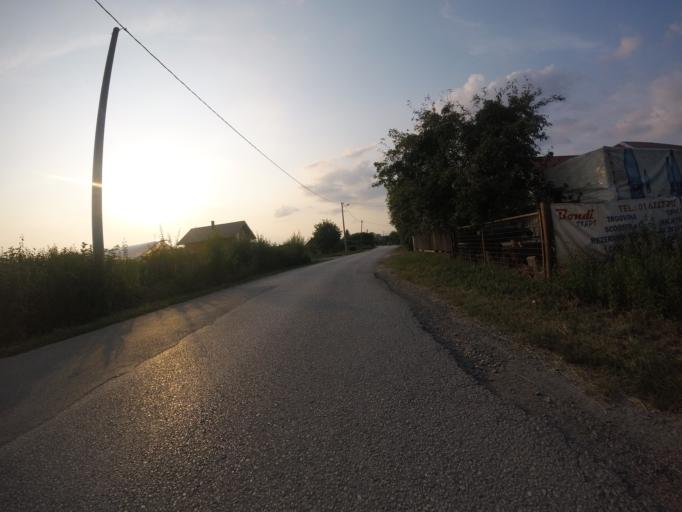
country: HR
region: Zagrebacka
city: Micevec
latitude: 45.7487
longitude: 16.1368
